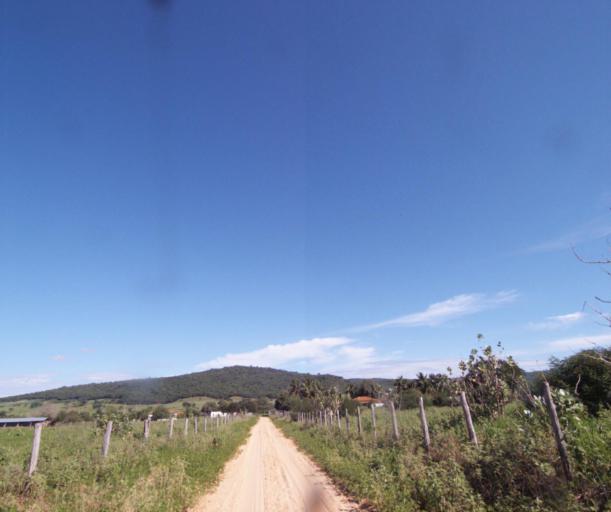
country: BR
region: Bahia
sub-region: Sao Felix Do Coribe
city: Santa Maria da Vitoria
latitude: -13.6180
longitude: -44.4136
